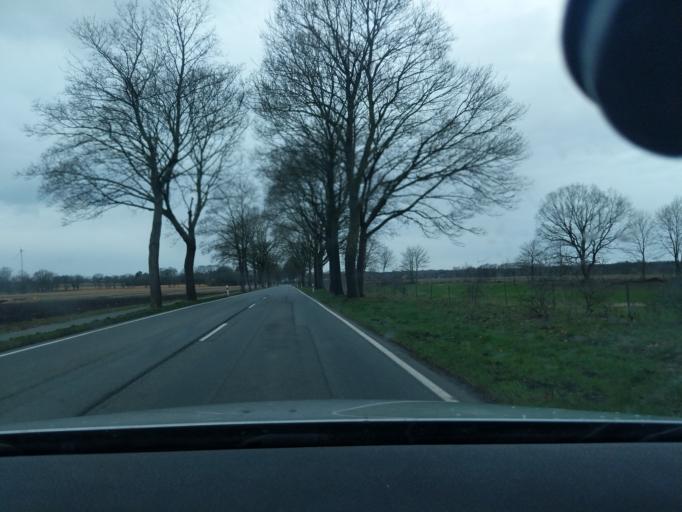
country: DE
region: Lower Saxony
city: Kutenholz
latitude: 53.4912
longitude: 9.2909
